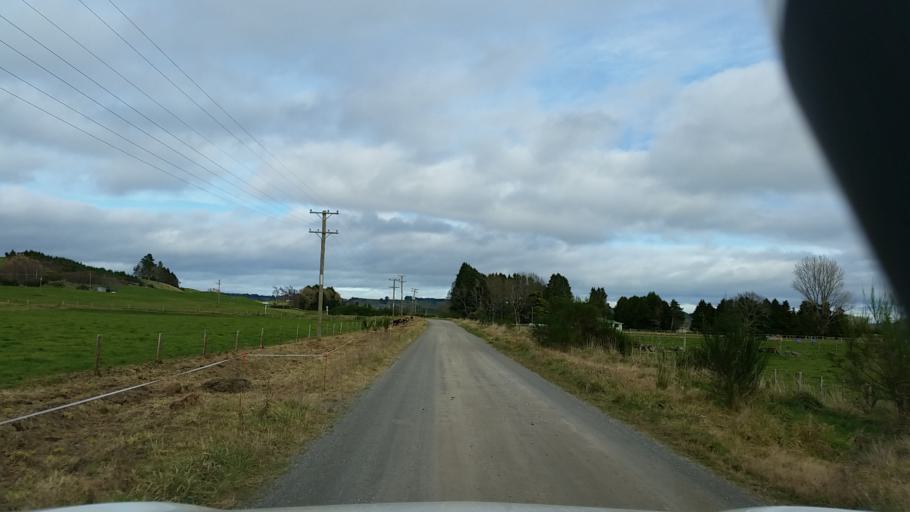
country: NZ
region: Bay of Plenty
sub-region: Whakatane District
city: Murupara
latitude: -38.2902
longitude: 176.5460
